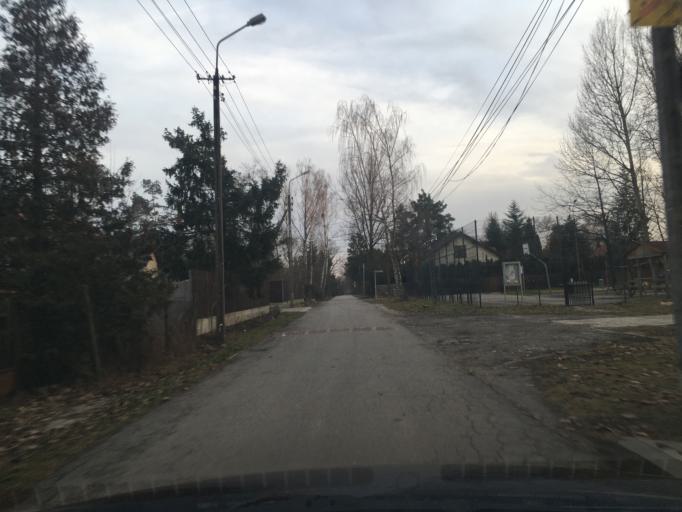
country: PL
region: Masovian Voivodeship
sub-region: Powiat piaseczynski
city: Lesznowola
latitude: 52.0388
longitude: 20.9567
